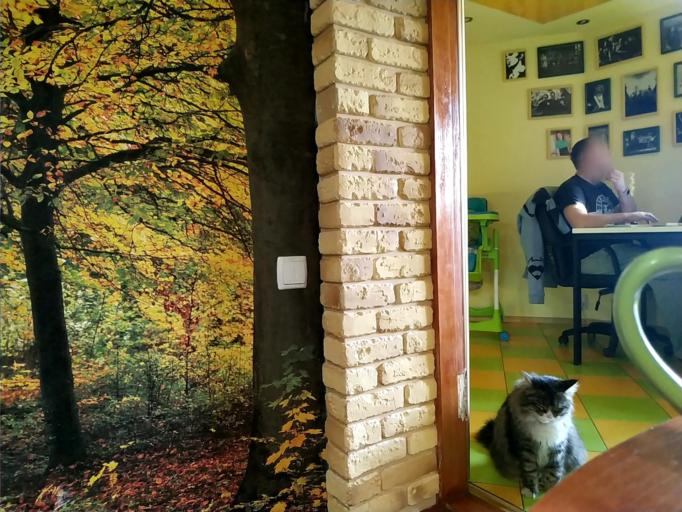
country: RU
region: Jaroslavl
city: Krasnyy Profintern
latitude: 57.8856
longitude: 40.5902
